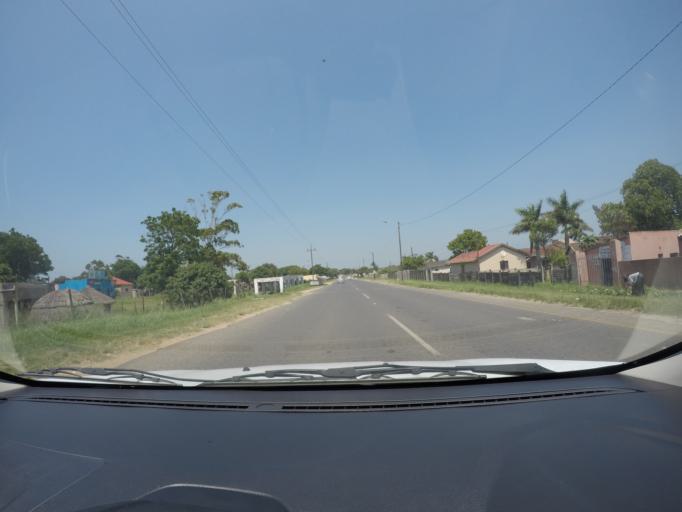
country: ZA
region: KwaZulu-Natal
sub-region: uThungulu District Municipality
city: eSikhawini
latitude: -28.8713
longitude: 31.9234
